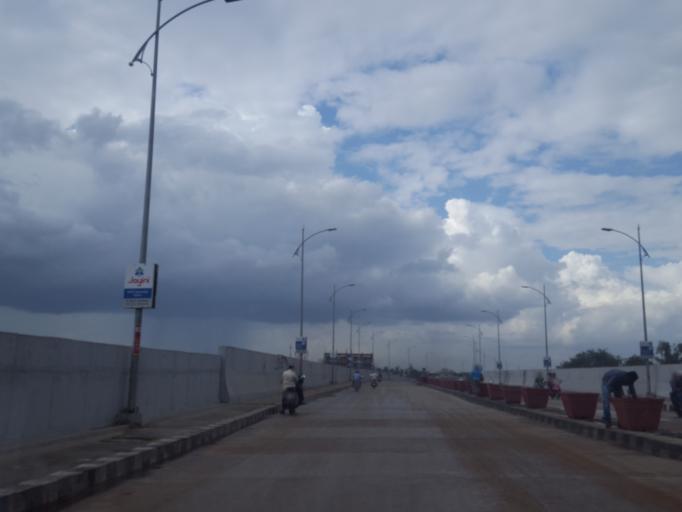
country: IN
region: Telangana
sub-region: Medak
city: Serilingampalle
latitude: 17.4806
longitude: 78.3110
